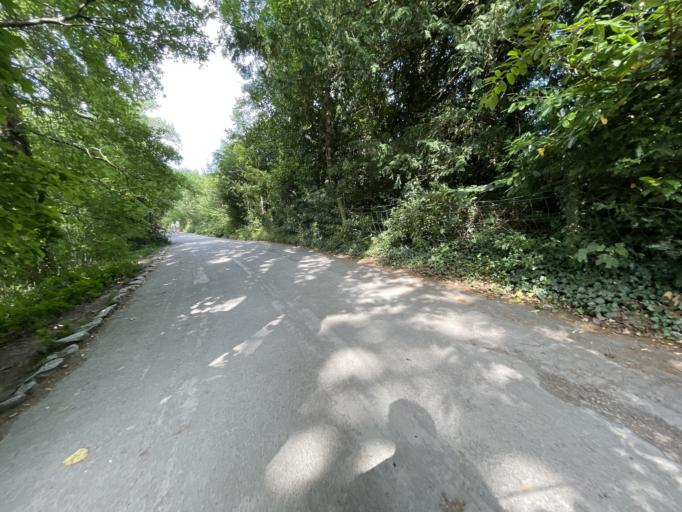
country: GB
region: England
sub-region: Cumbria
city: Keswick
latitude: 54.5928
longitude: -3.1404
